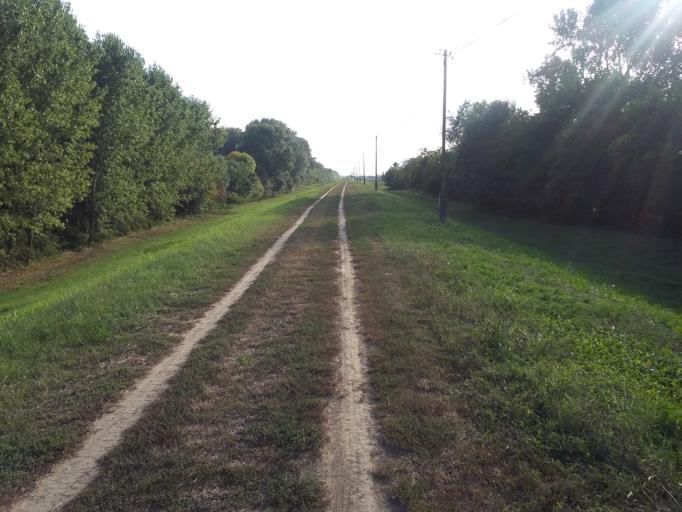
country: HU
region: Csongrad
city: Szeged
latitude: 46.2052
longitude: 20.1165
